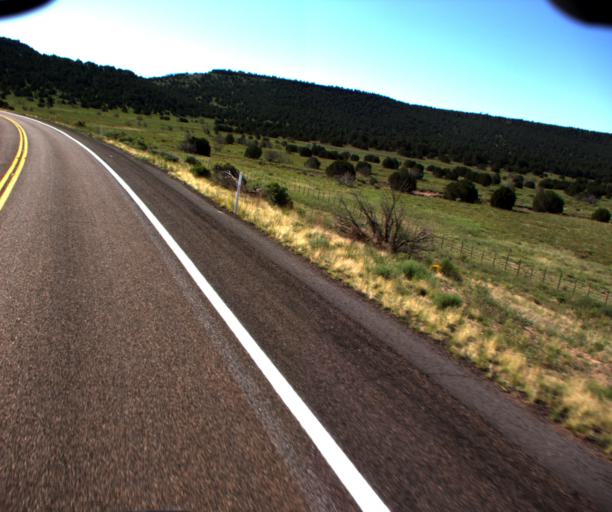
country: US
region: Arizona
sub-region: Apache County
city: Eagar
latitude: 34.0945
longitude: -109.2122
